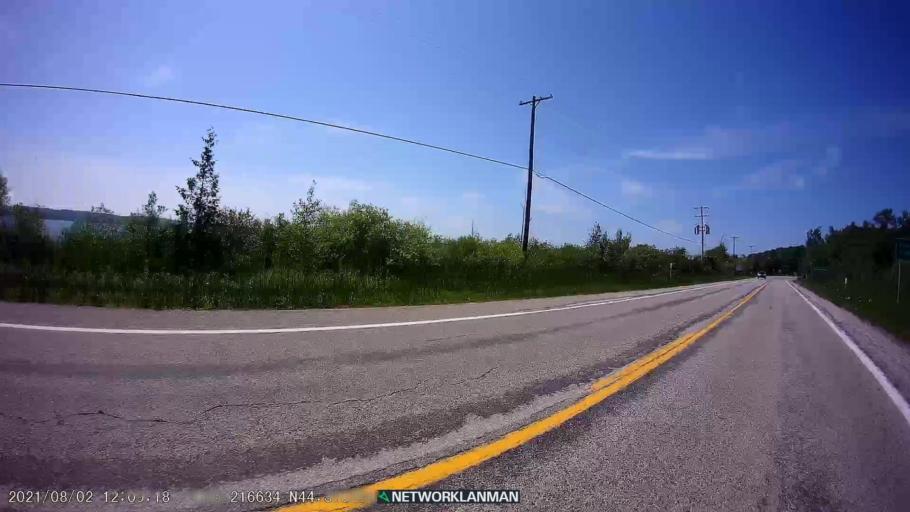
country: US
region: Michigan
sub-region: Manistee County
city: Manistee
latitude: 44.3704
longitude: -86.2169
